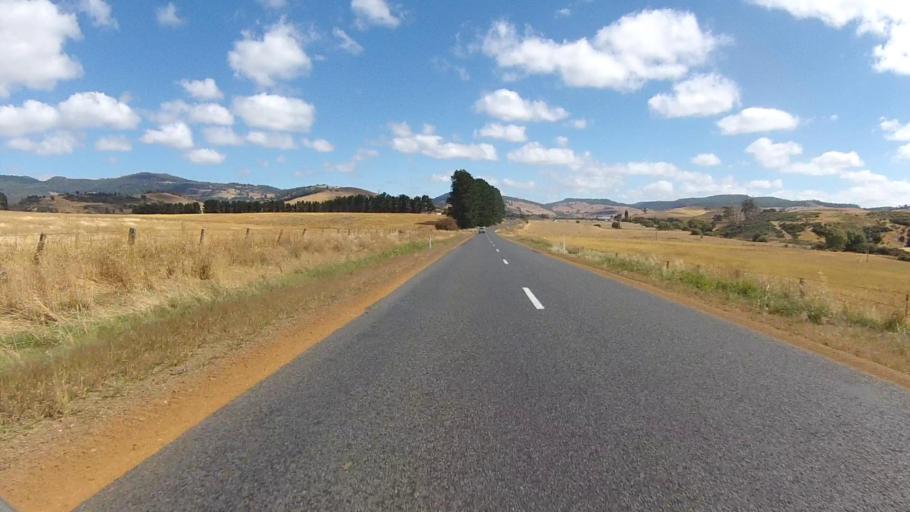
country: AU
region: Tasmania
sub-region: Brighton
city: Bridgewater
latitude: -42.5519
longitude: 147.3799
